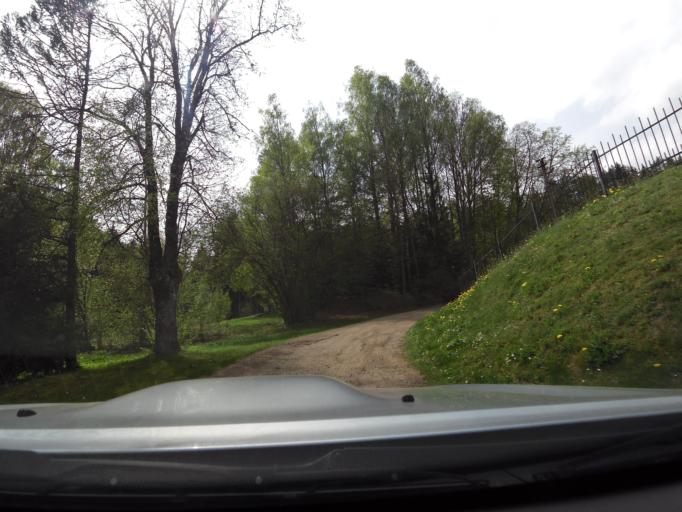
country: LT
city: Salcininkai
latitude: 54.4267
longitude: 25.3105
